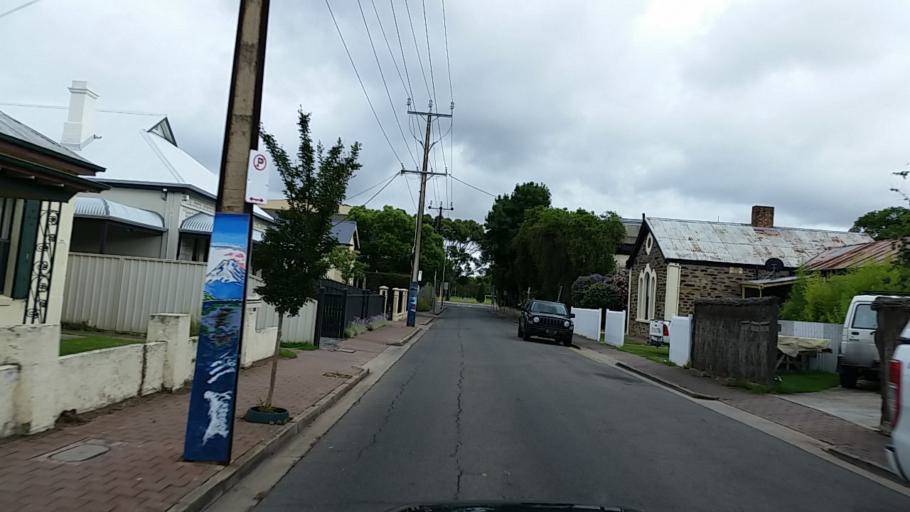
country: AU
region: South Australia
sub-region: Unley
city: Unley
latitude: -34.9422
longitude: 138.6079
